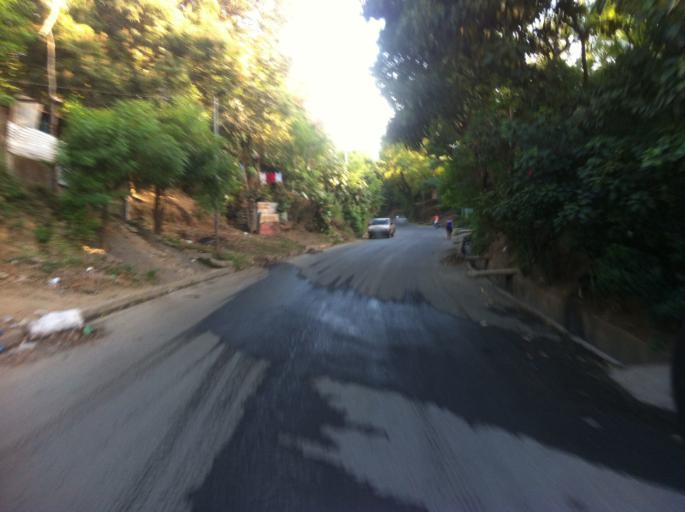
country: NI
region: Managua
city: Ciudad Sandino
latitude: 12.1054
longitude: -86.3091
